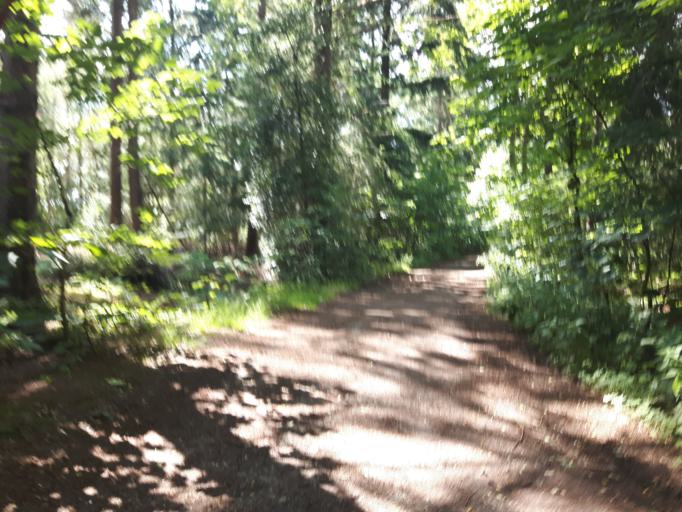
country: NL
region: Overijssel
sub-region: Gemeente Haaksbergen
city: Haaksbergen
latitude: 52.1851
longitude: 6.7627
